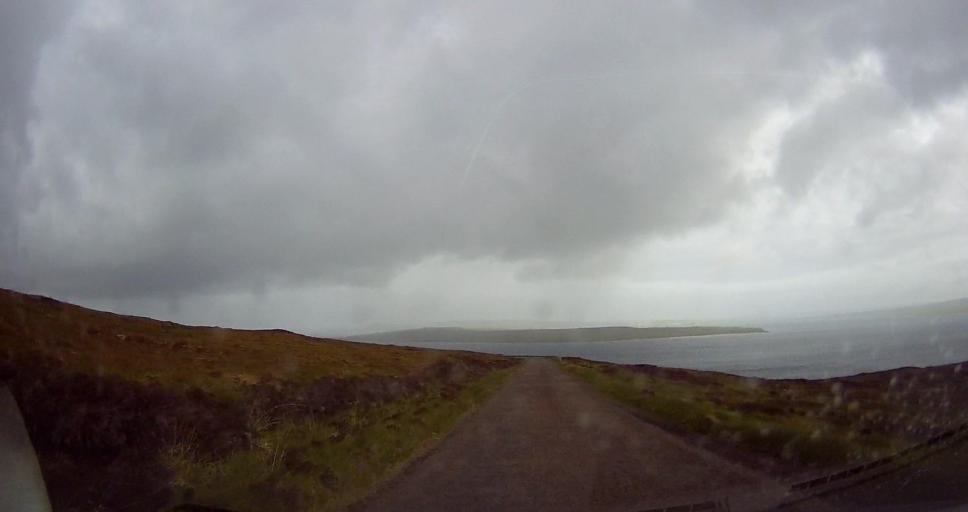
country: GB
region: Scotland
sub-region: Orkney Islands
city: Stromness
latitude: 58.8984
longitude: -3.2739
